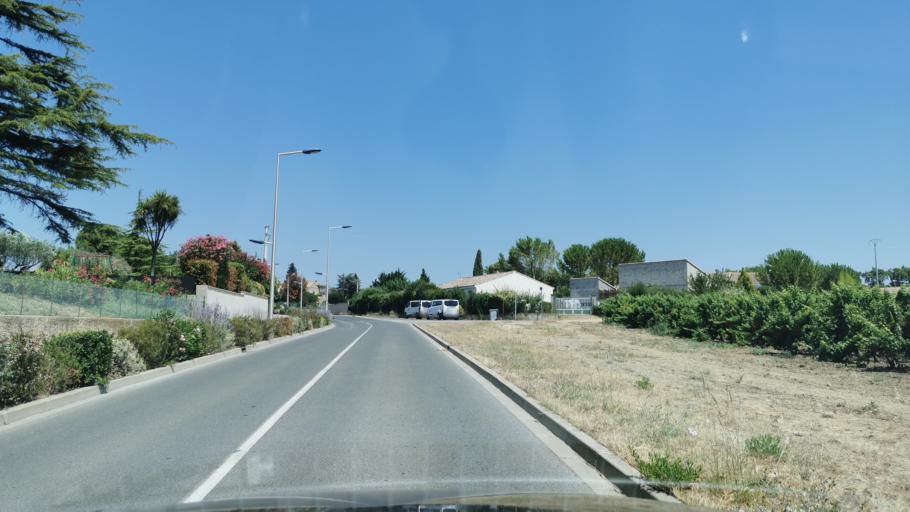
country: FR
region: Languedoc-Roussillon
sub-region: Departement de l'Herault
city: Cazouls-les-Beziers
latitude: 43.3861
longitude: 3.1046
